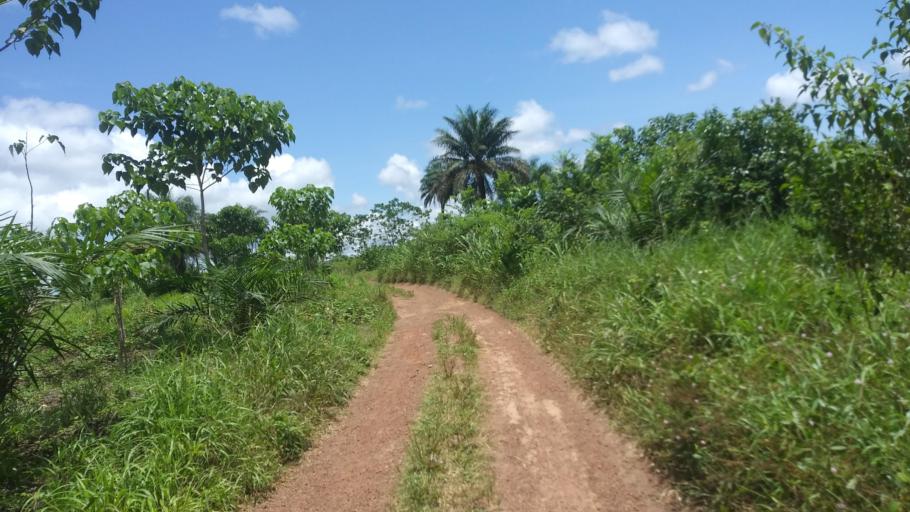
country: SL
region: Northern Province
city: Makeni
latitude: 8.8884
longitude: -12.0126
